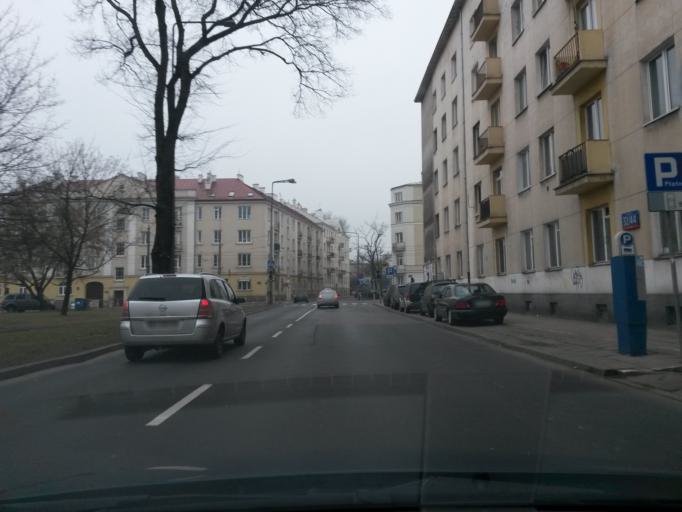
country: PL
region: Masovian Voivodeship
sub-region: Warszawa
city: Ochota
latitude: 52.2198
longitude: 20.9894
